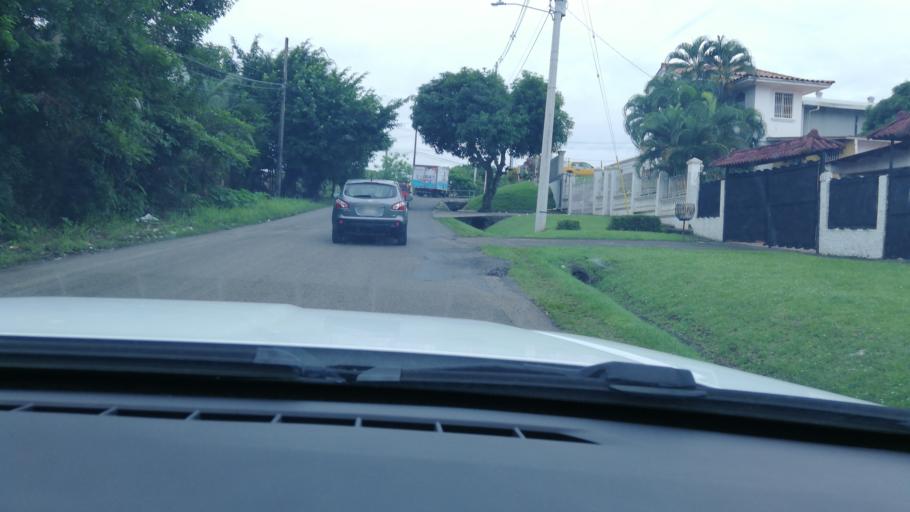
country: PA
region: Panama
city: Las Cumbres
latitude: 9.0749
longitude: -79.5198
